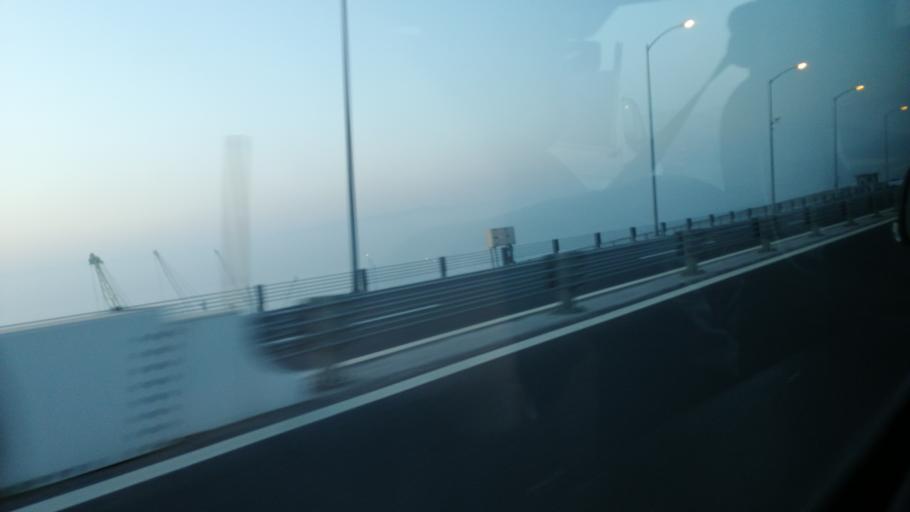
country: TR
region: Kocaeli
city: Tavsanli
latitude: 40.7668
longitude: 29.5178
